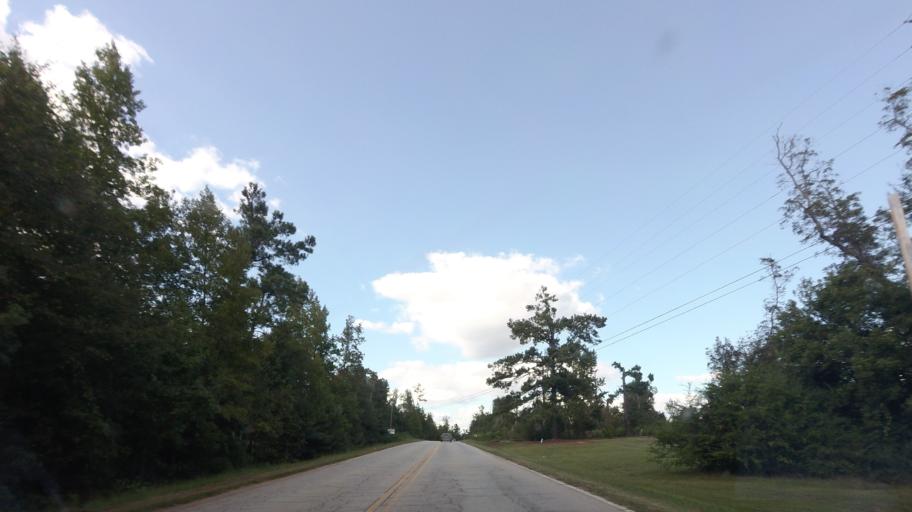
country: US
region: Georgia
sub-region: Lamar County
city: Barnesville
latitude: 33.0775
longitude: -84.1552
